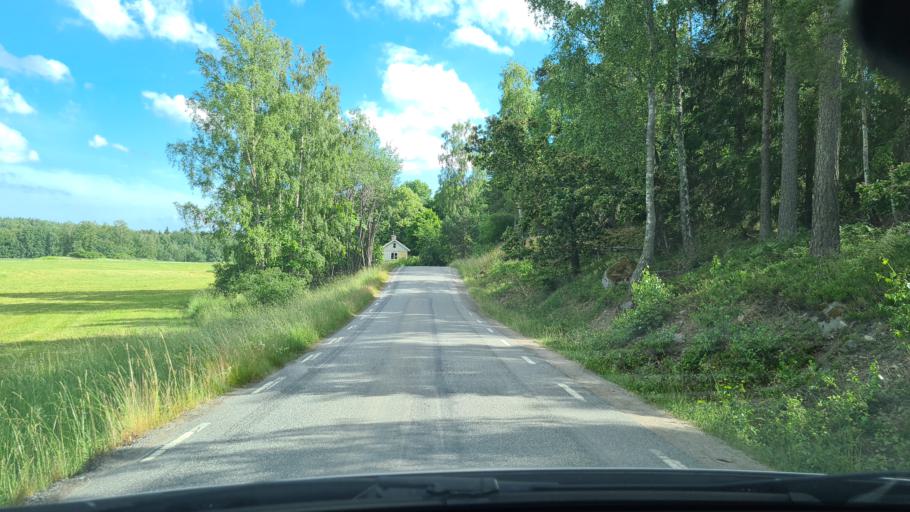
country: SE
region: Stockholm
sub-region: Varmdo Kommun
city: Mortnas
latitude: 59.4095
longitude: 18.4537
